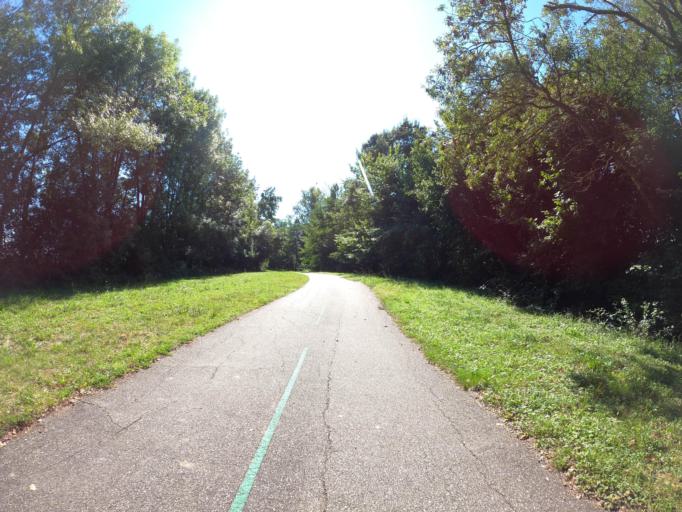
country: FR
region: Aquitaine
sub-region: Departement du Lot-et-Garonne
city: Bias
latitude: 44.4047
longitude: 0.6638
